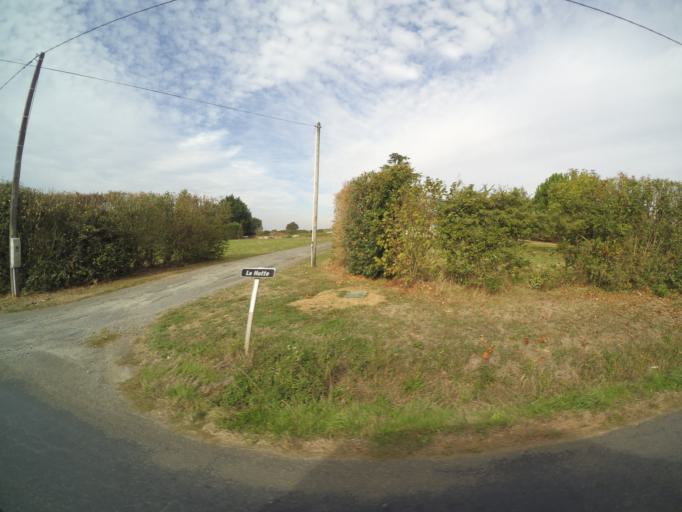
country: FR
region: Pays de la Loire
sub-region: Departement de Maine-et-Loire
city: Andreze
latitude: 47.1761
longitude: -0.9423
